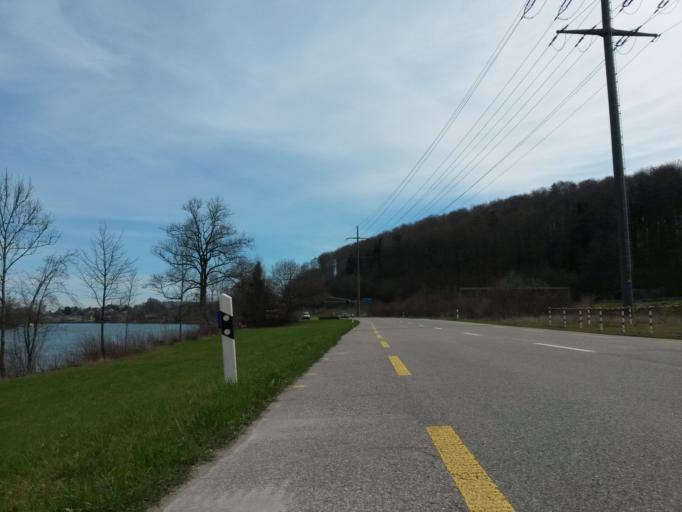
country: CH
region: Solothurn
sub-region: Bezirk Solothurn
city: Solothurn
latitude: 47.1952
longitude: 7.5165
